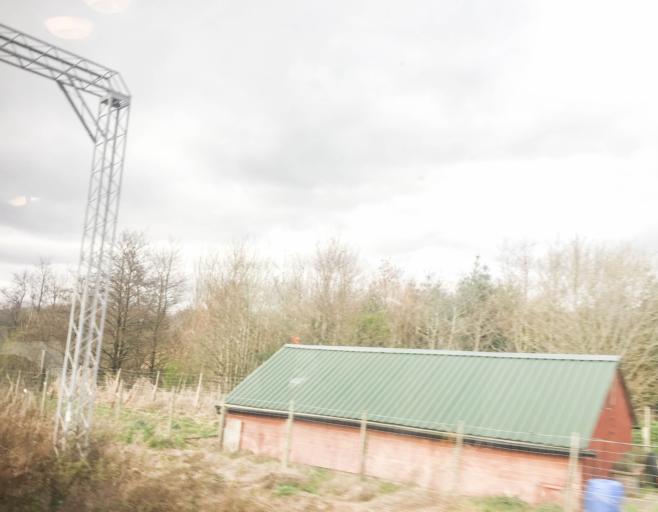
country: GB
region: Scotland
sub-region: Argyll and Bute
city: Cardross
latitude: 55.9615
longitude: -4.6574
